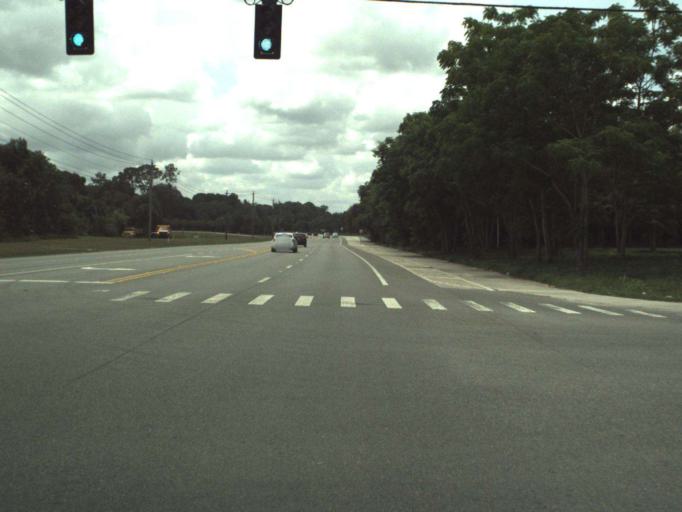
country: US
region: Florida
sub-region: Volusia County
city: Daytona Beach
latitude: 29.1805
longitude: -81.0423
